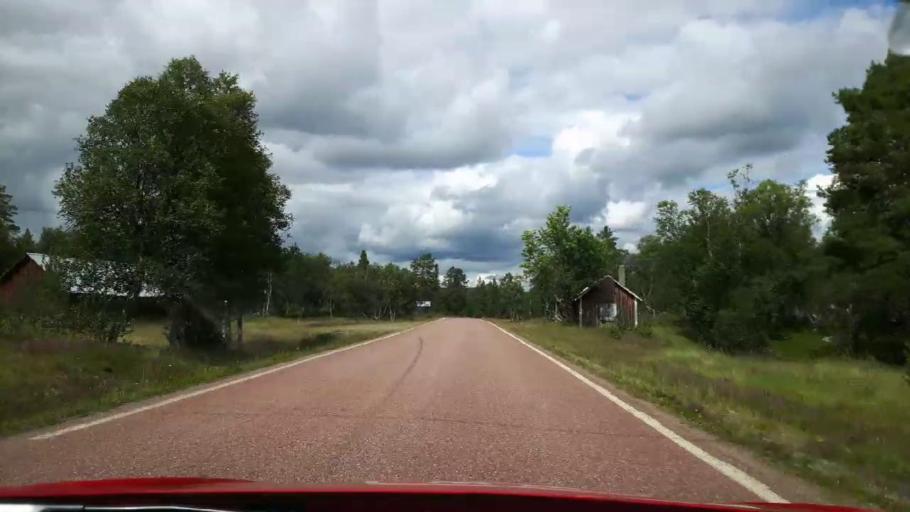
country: NO
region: Hedmark
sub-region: Trysil
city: Innbygda
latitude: 62.0946
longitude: 12.9730
